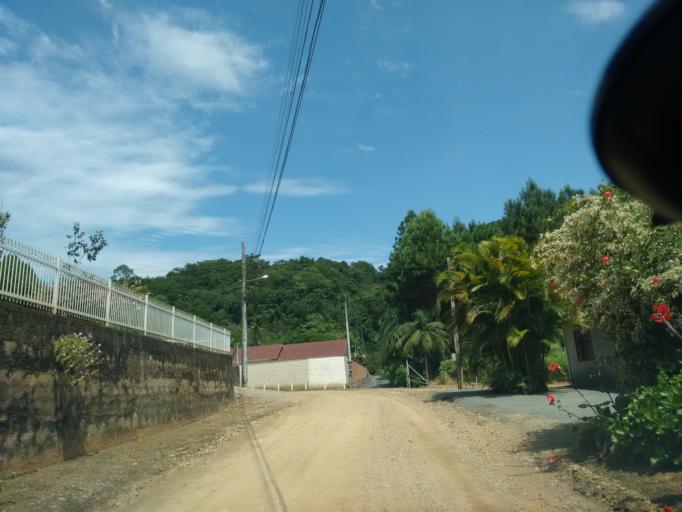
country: BR
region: Santa Catarina
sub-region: Indaial
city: Indaial
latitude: -26.8509
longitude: -49.1641
